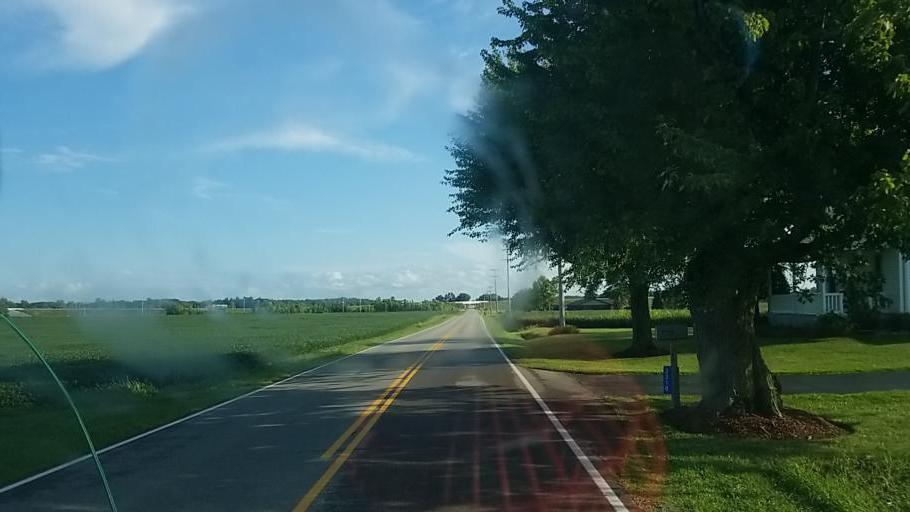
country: US
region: Ohio
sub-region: Crawford County
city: Bucyrus
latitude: 40.8238
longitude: -83.0931
